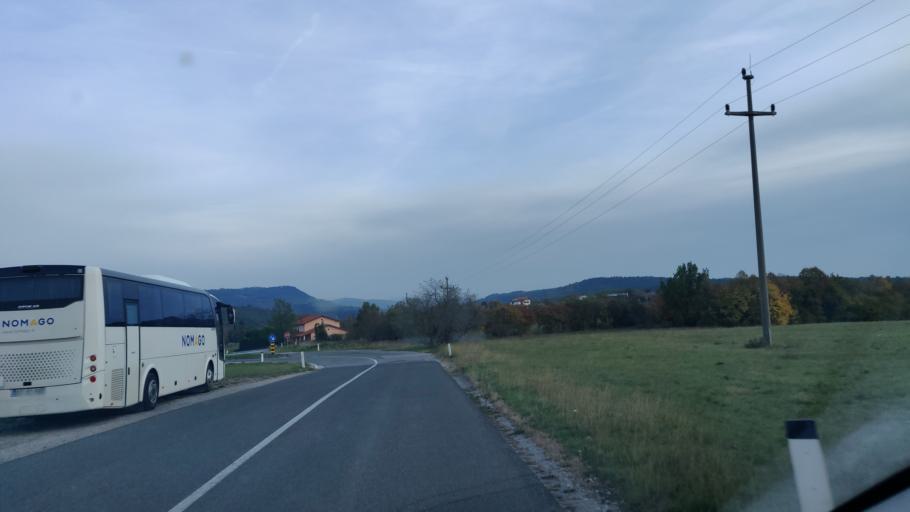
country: SI
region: Ajdovscina
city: Lokavec
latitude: 45.8179
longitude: 13.8440
